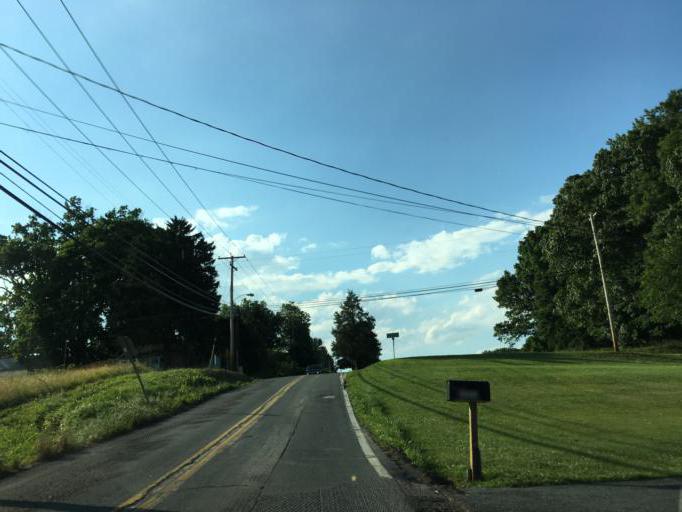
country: US
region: Maryland
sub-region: Baltimore County
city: Kingsville
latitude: 39.4490
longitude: -76.4415
